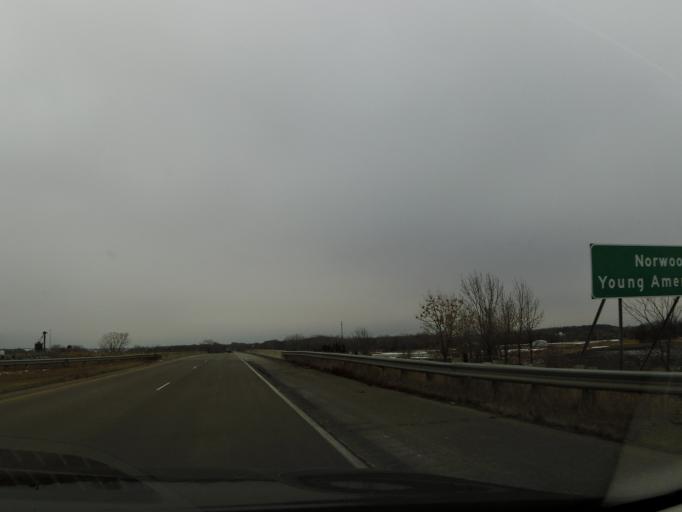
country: US
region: Minnesota
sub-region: Carver County
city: Cologne
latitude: 44.7671
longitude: -93.7887
